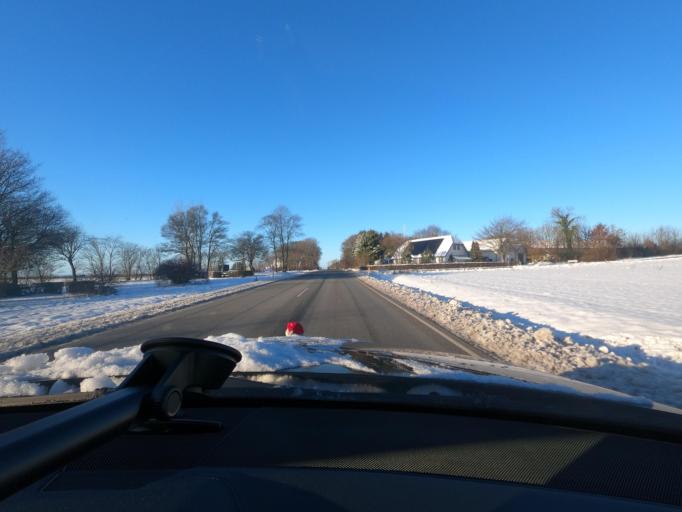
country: DK
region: South Denmark
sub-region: Aabenraa Kommune
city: Rodekro
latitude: 55.0896
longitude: 9.2055
